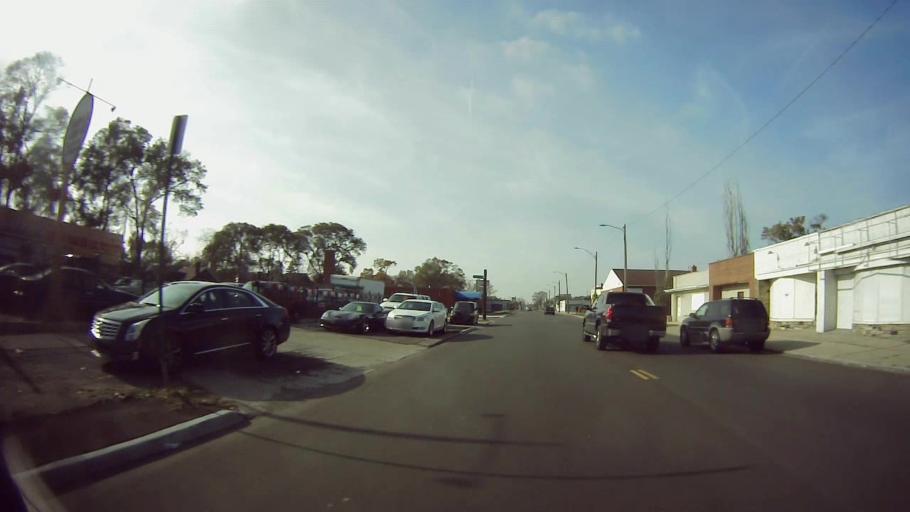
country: US
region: Michigan
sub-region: Oakland County
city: Oak Park
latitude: 42.4094
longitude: -83.1746
